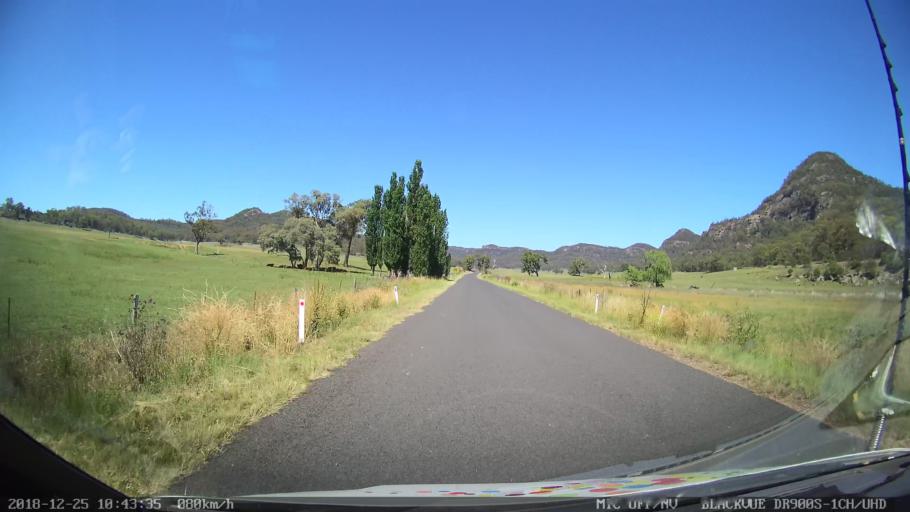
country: AU
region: New South Wales
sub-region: Upper Hunter Shire
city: Merriwa
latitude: -32.4231
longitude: 150.3110
